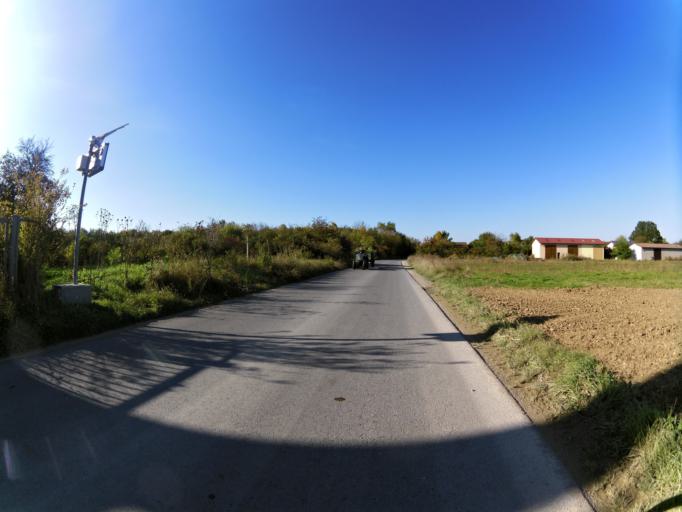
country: DE
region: Bavaria
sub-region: Regierungsbezirk Unterfranken
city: Sommerhausen
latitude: 49.6944
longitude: 10.0384
